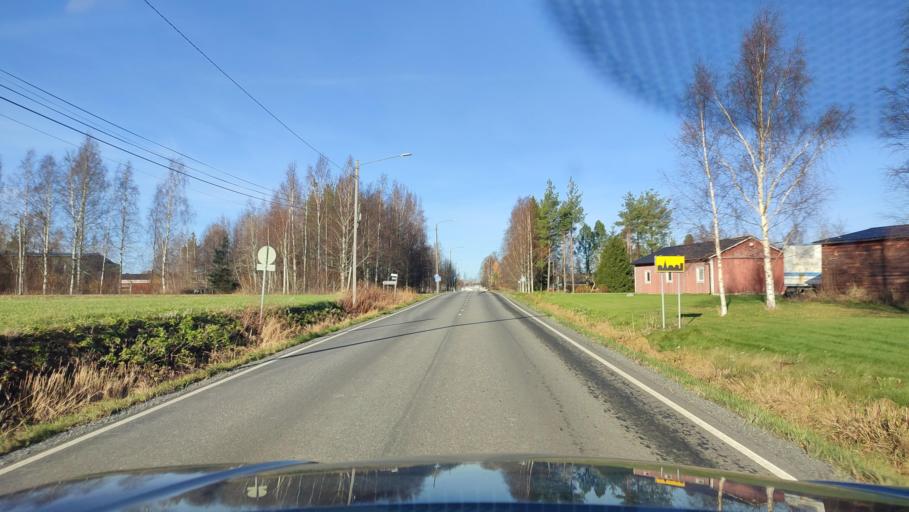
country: FI
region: Southern Ostrobothnia
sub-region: Suupohja
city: Karijoki
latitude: 62.3020
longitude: 21.7145
